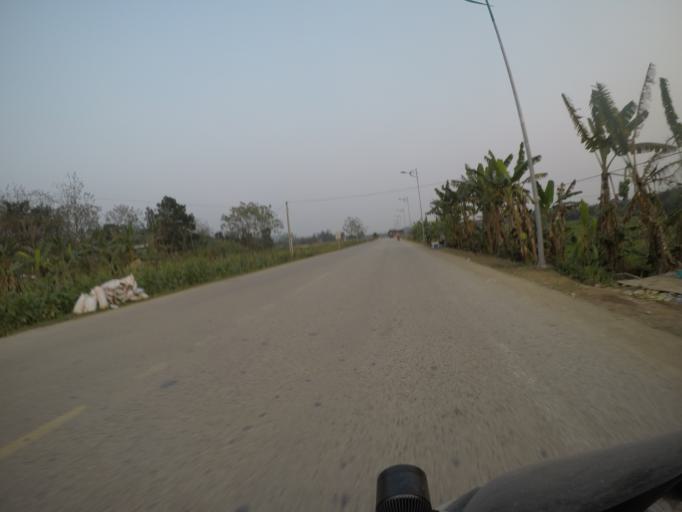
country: VN
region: Vinh Phuc
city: Trai Ngau
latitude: 21.4384
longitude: 105.5749
